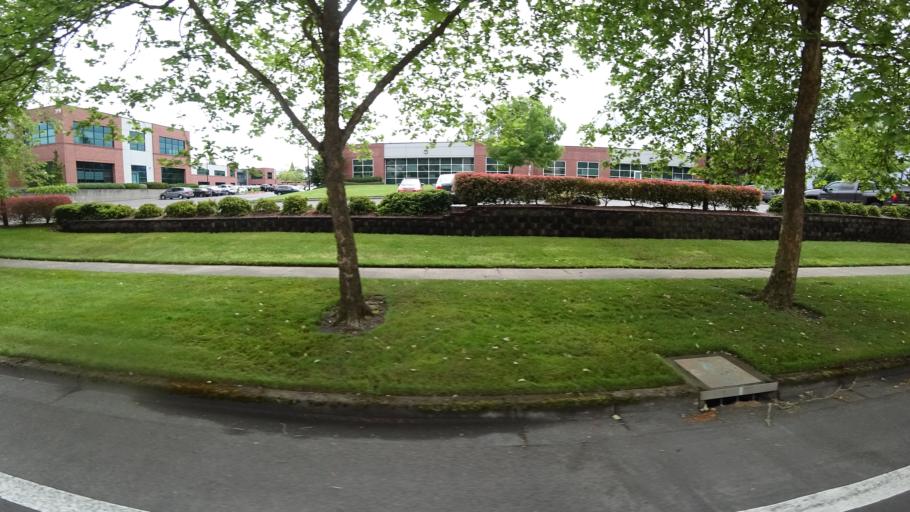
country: US
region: Oregon
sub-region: Washington County
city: Rockcreek
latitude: 45.5366
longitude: -122.8883
